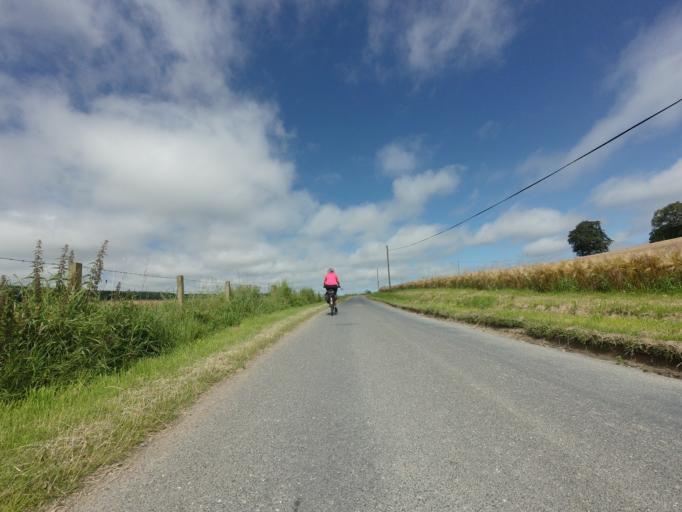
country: GB
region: Scotland
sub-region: Aberdeenshire
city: Turriff
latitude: 57.5666
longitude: -2.4949
